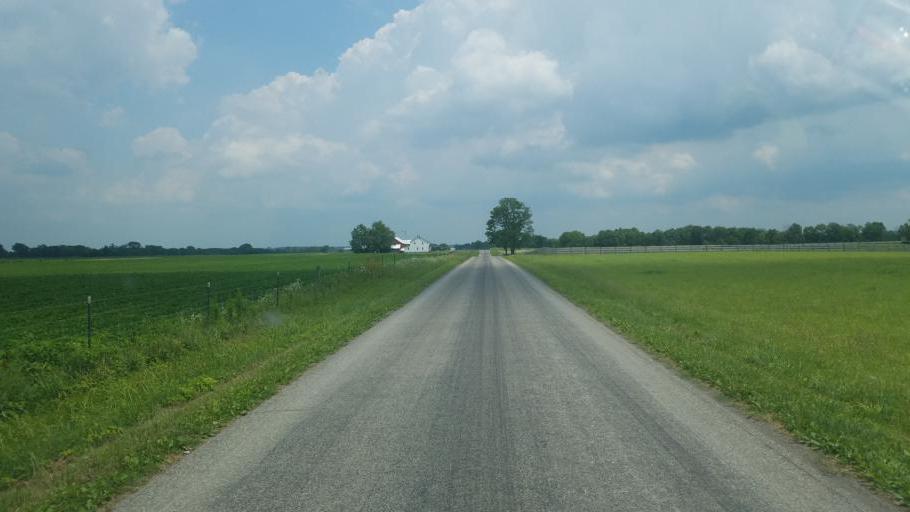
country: US
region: Ohio
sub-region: Hardin County
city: Kenton
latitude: 40.5923
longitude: -83.6349
